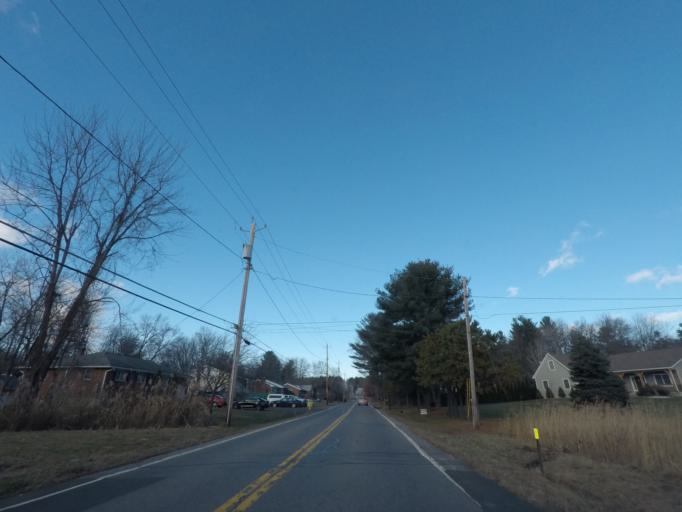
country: US
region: New York
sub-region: Saratoga County
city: Mechanicville
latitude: 42.8719
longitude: -73.7430
